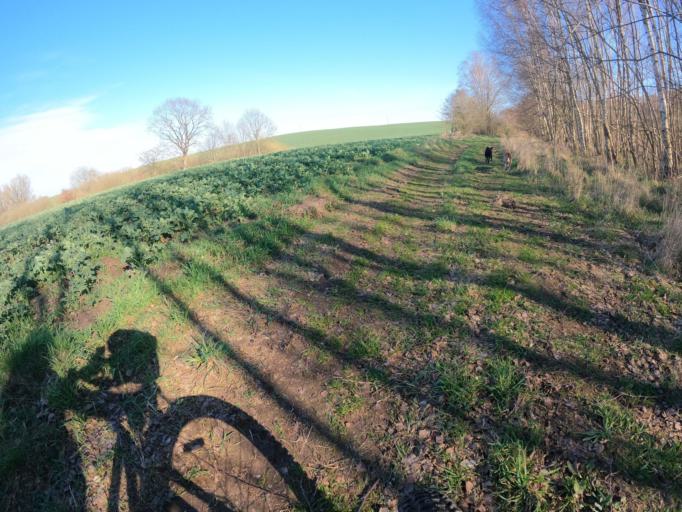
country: PL
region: West Pomeranian Voivodeship
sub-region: Powiat kolobrzeski
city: Ryman
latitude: 54.0119
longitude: 15.4798
